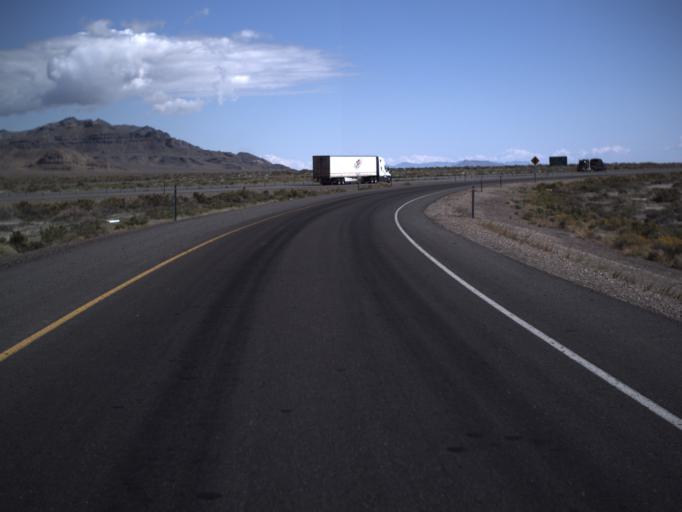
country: US
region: Utah
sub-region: Tooele County
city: Wendover
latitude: 40.7449
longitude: -114.0167
